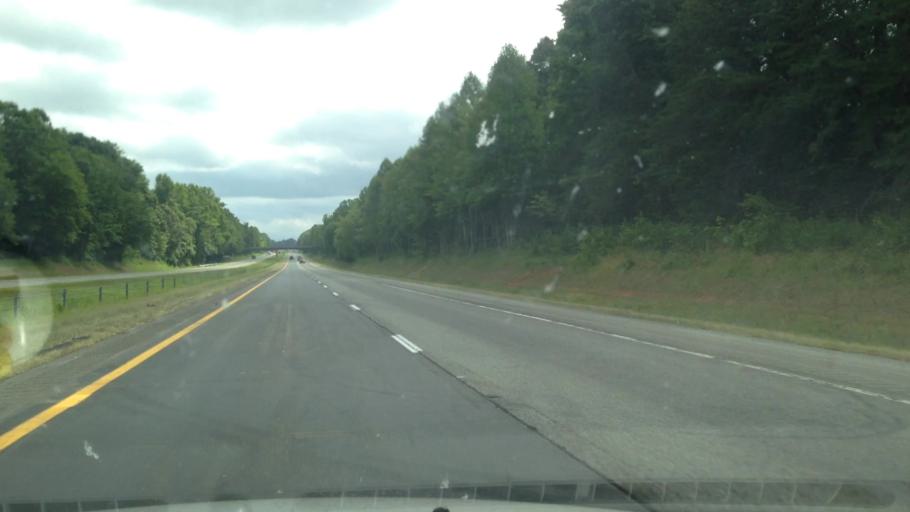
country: US
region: North Carolina
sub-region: Rockingham County
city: Reidsville
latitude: 36.4477
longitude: -79.5621
